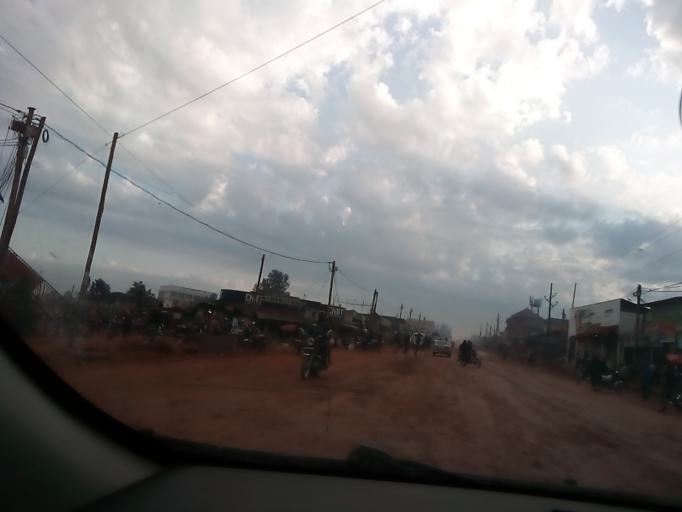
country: UG
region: Central Region
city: Masaka
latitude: -0.3177
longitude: 31.7595
